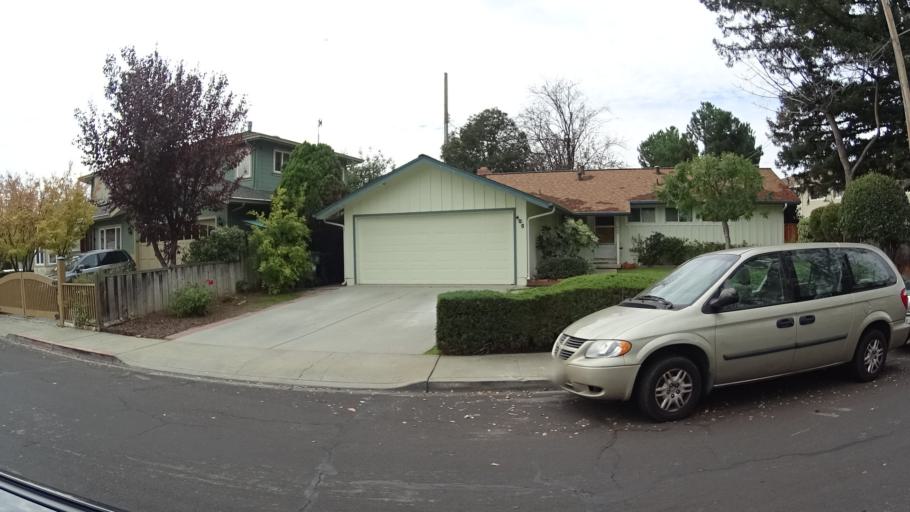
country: US
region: California
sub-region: Santa Clara County
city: Santa Clara
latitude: 37.3395
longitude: -121.9530
